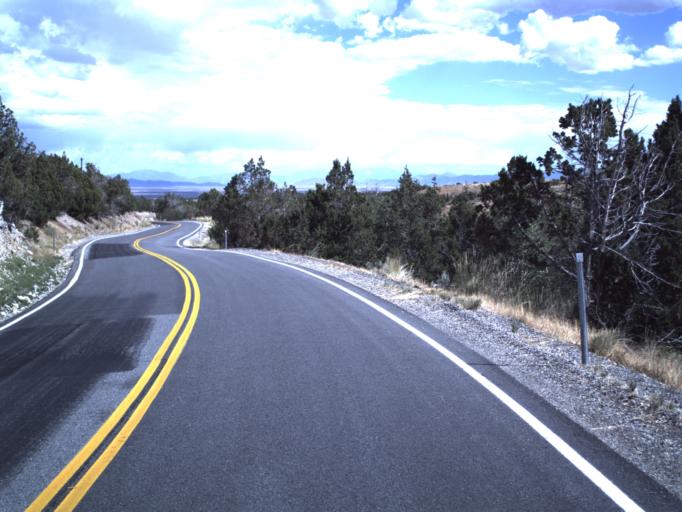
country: US
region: Utah
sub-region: Tooele County
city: Grantsville
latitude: 40.3382
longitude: -112.5345
